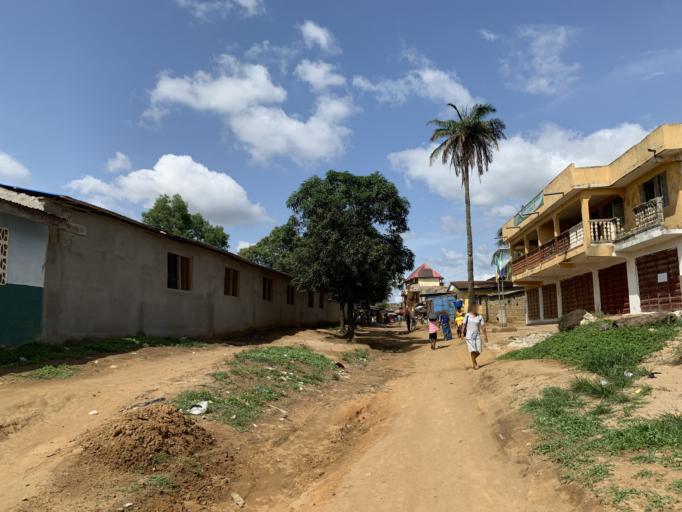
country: SL
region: Western Area
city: Waterloo
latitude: 8.3348
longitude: -13.0444
